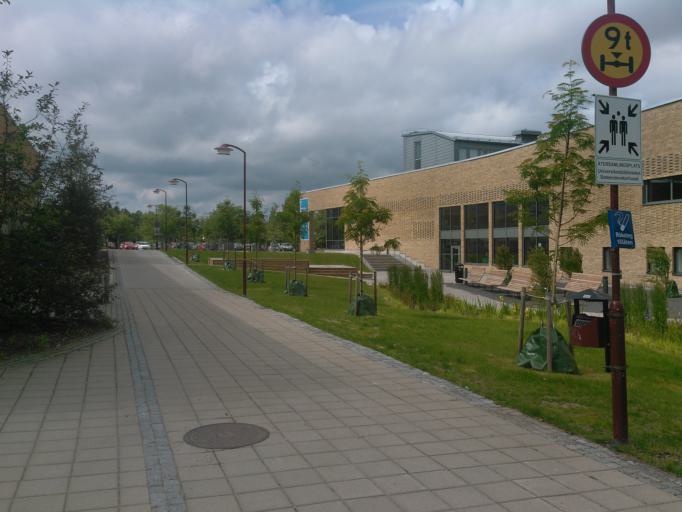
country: SE
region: Vaesterbotten
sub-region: Umea Kommun
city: Umea
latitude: 63.8221
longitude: 20.3073
